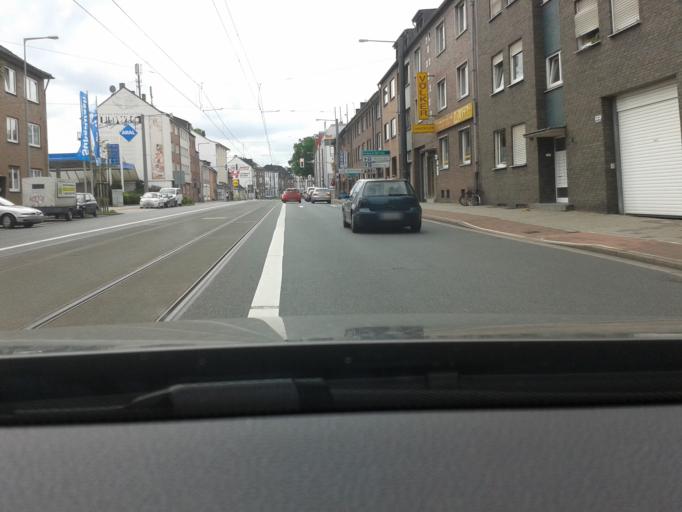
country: DE
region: North Rhine-Westphalia
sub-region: Regierungsbezirk Dusseldorf
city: Oberhausen
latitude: 51.4676
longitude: 6.8641
